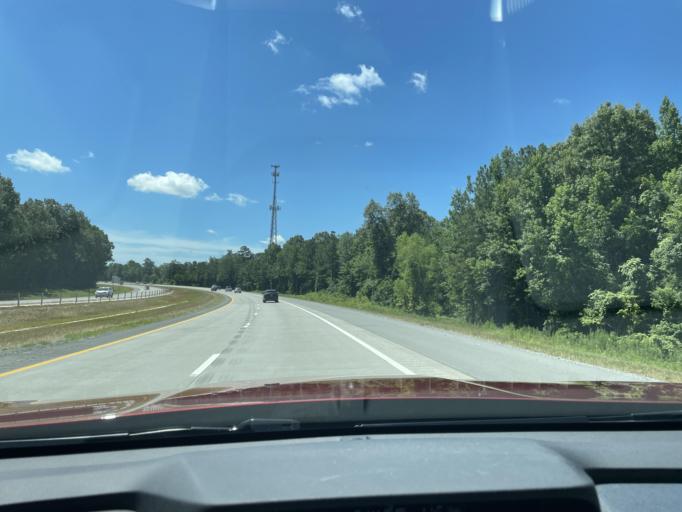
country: US
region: Arkansas
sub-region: Jefferson County
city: Sulphur Springs
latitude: 34.2017
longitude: -92.0723
